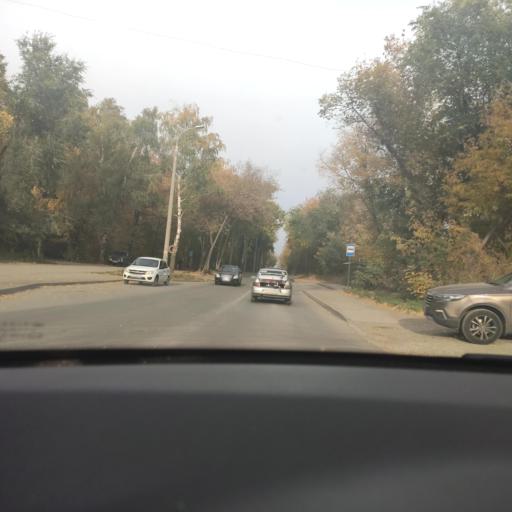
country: RU
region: Samara
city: Samara
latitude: 53.2232
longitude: 50.2069
